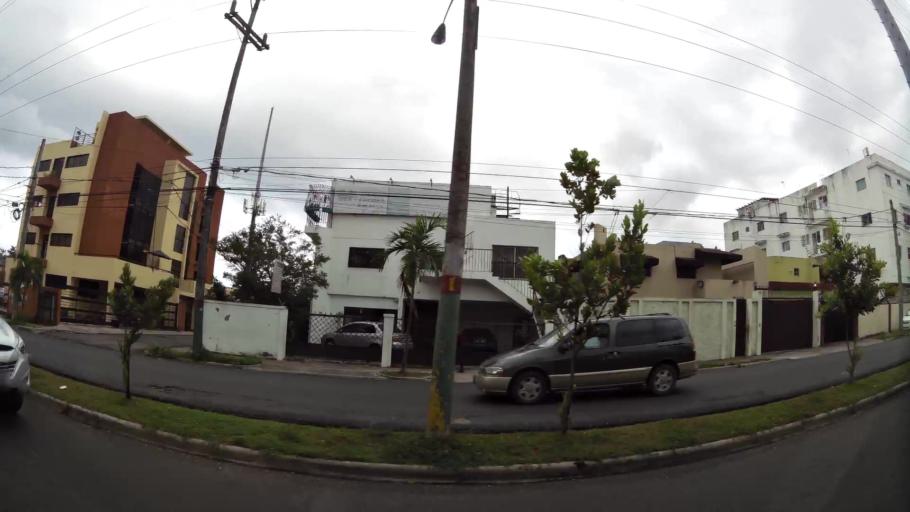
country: DO
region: Nacional
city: La Agustina
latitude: 18.5018
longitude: -69.9421
